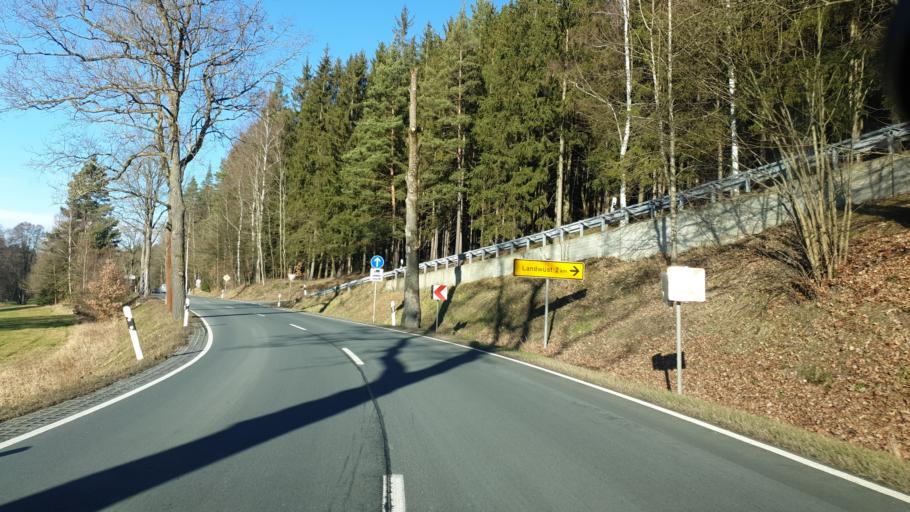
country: DE
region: Saxony
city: Markneukirchen
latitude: 50.2683
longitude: 12.3002
